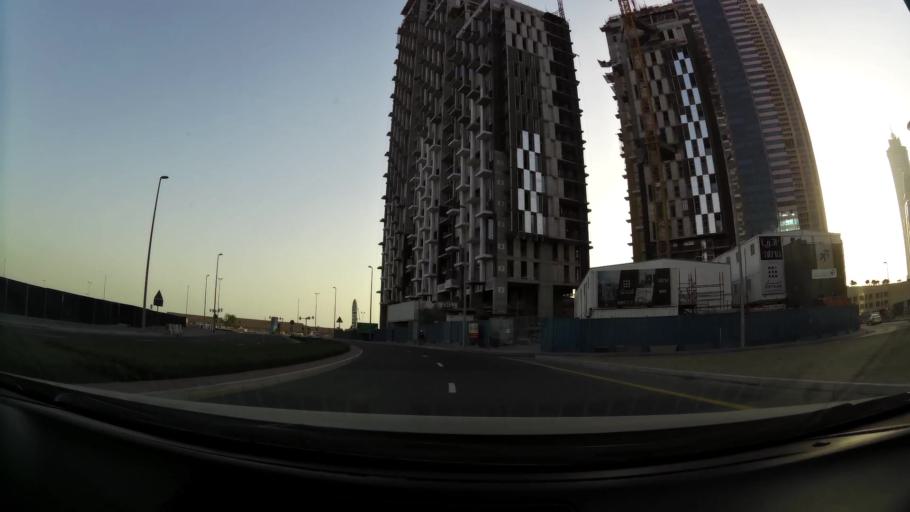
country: AE
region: Dubai
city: Dubai
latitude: 25.1803
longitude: 55.2651
